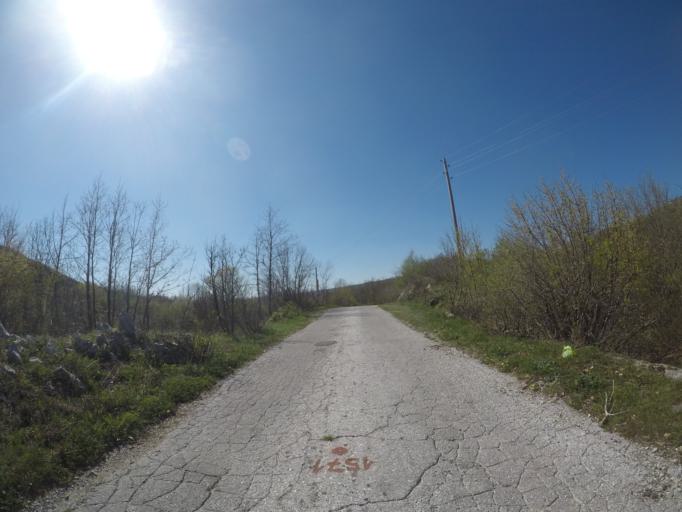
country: ME
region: Danilovgrad
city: Danilovgrad
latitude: 42.5391
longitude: 19.0114
